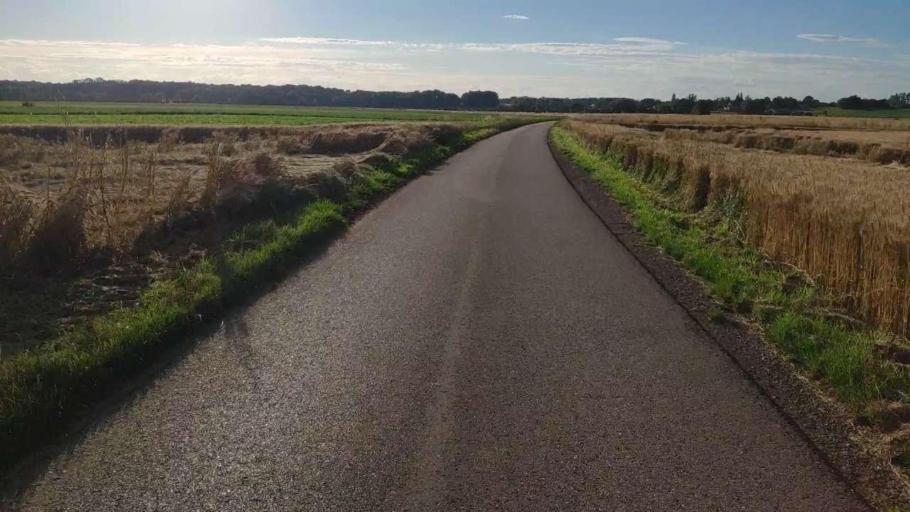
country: FR
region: Franche-Comte
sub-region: Departement du Jura
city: Bletterans
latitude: 46.7710
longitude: 5.5005
